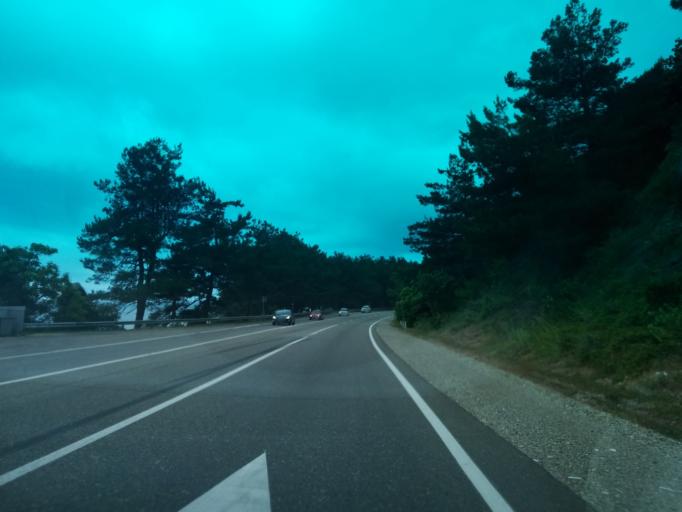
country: RU
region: Krasnodarskiy
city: Ol'ginka
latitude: 44.1847
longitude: 38.9223
